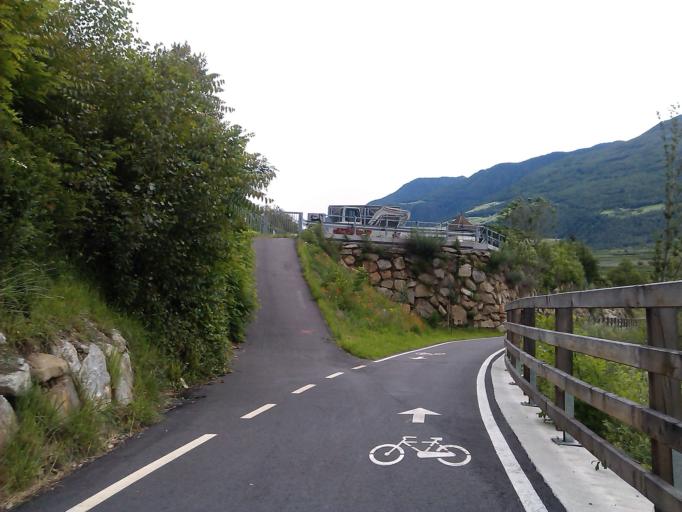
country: IT
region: Trentino-Alto Adige
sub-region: Bolzano
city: Laces
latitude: 46.6226
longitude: 10.8616
